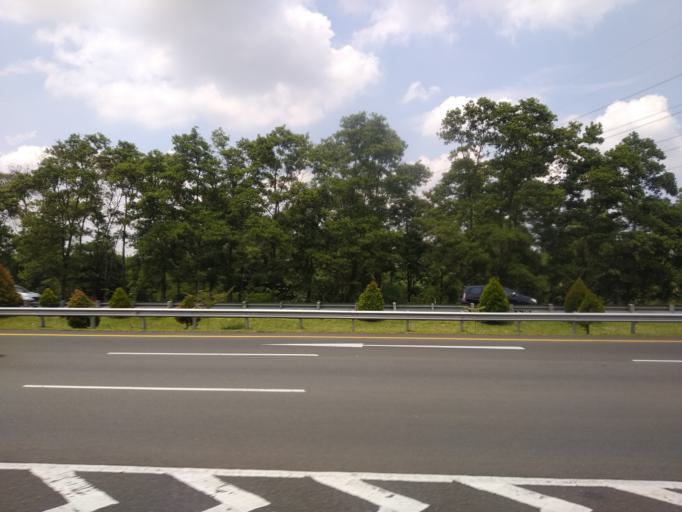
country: ID
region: West Java
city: Bogor
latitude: -6.5921
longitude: 106.8342
